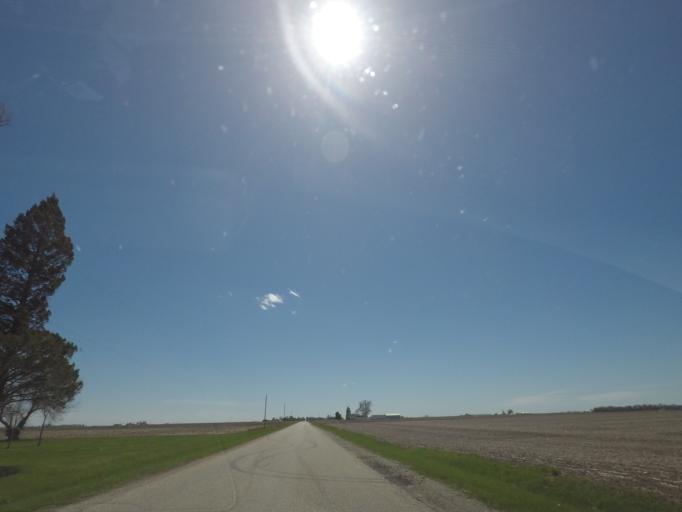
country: US
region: Illinois
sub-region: Logan County
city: Atlanta
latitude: 40.1699
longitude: -89.1937
